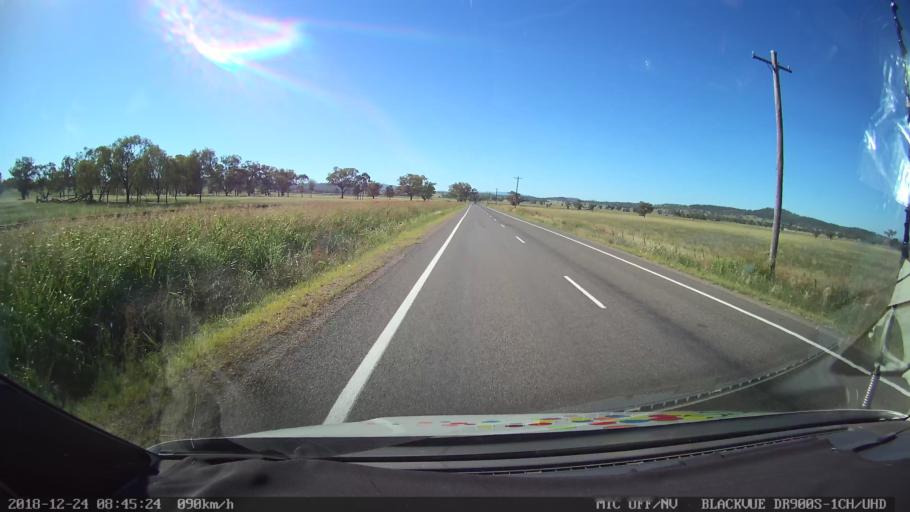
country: AU
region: New South Wales
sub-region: Liverpool Plains
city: Quirindi
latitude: -31.4145
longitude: 150.6519
